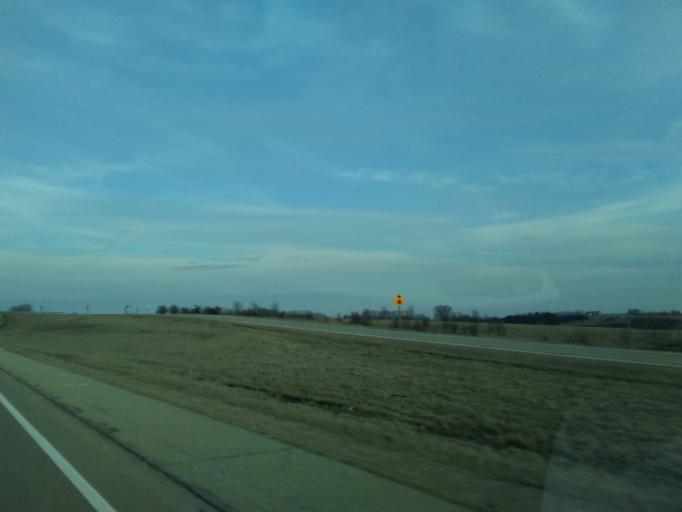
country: US
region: Wisconsin
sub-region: Dane County
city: Verona
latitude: 42.9874
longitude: -89.5858
